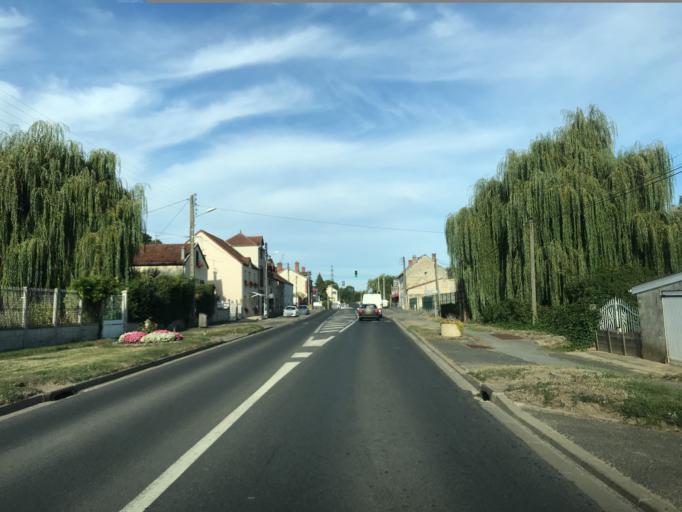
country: FR
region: Champagne-Ardenne
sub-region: Departement de la Marne
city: Damery
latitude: 49.0611
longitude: 3.8758
